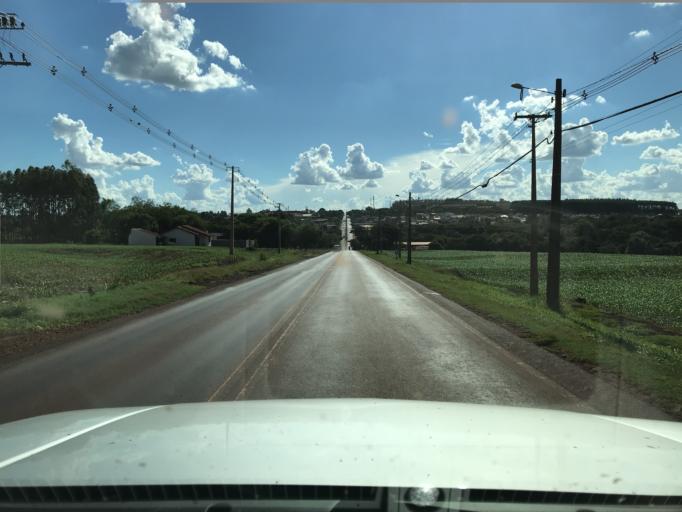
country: BR
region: Parana
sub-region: Palotina
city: Palotina
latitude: -24.2770
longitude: -53.8171
